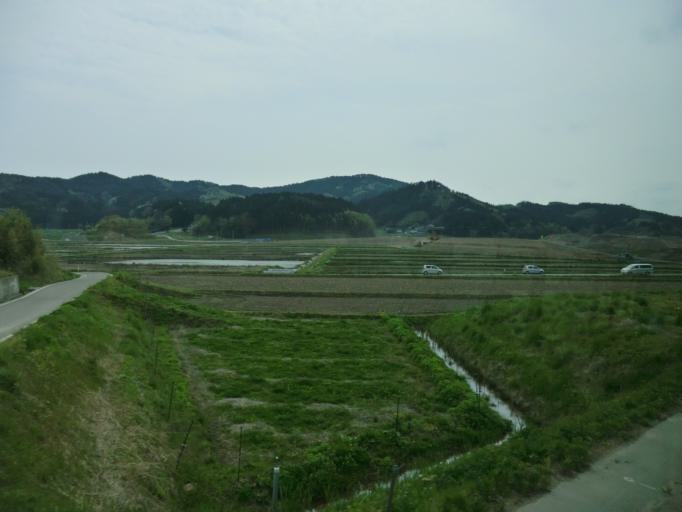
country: JP
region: Iwate
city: Ofunato
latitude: 38.9965
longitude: 141.6953
